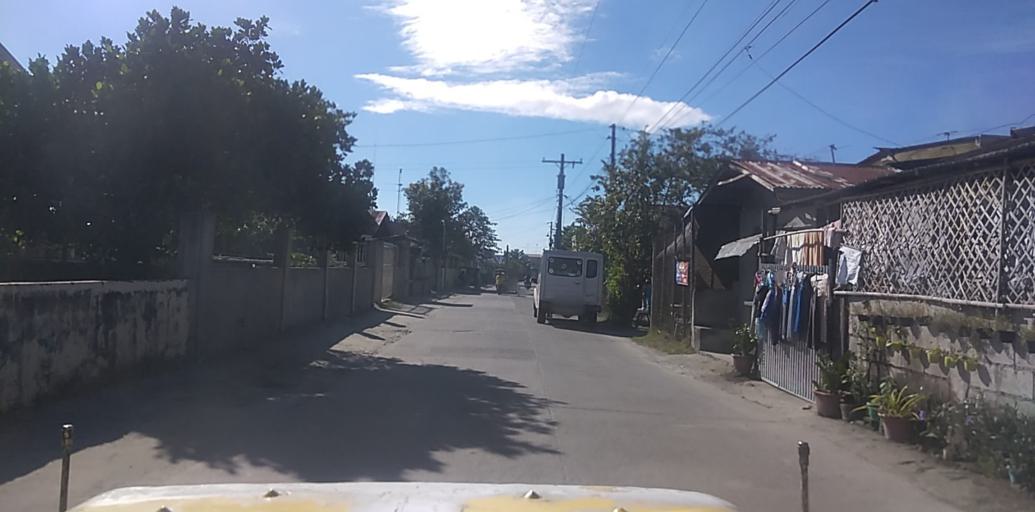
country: PH
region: Central Luzon
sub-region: Province of Pampanga
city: San Patricio
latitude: 15.1049
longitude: 120.7135
